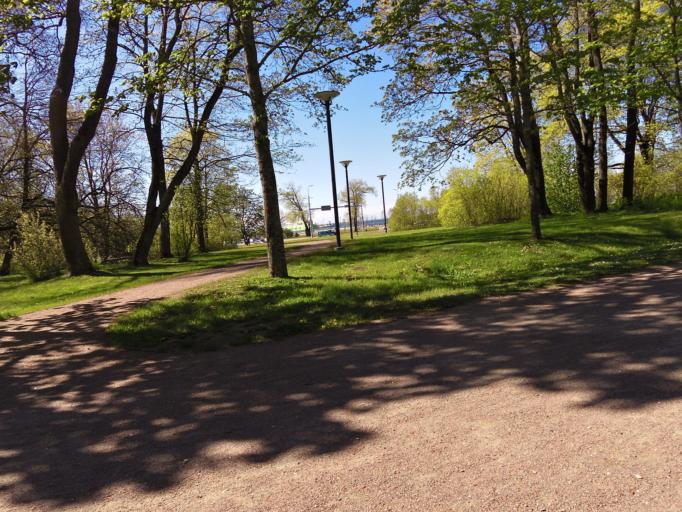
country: EE
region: Harju
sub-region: Tallinna linn
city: Tallinn
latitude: 59.4419
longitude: 24.7930
